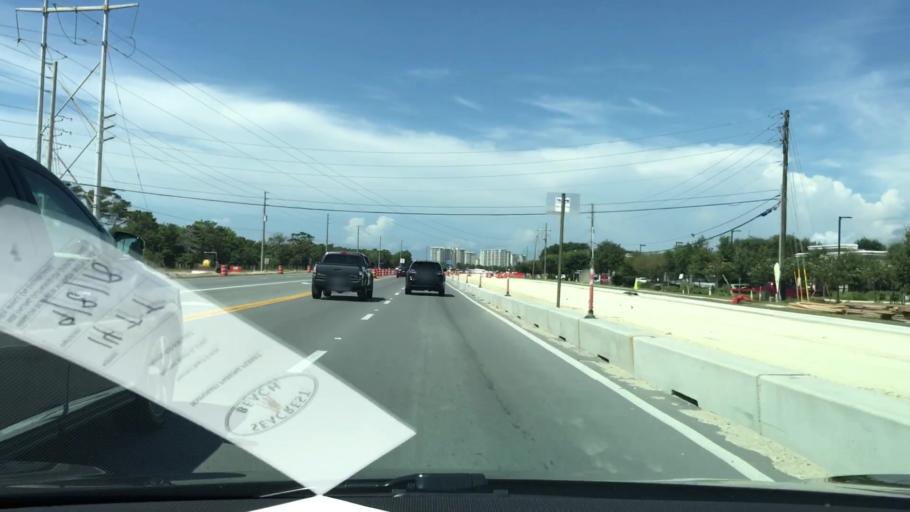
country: US
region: Florida
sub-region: Okaloosa County
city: Destin
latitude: 30.3878
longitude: -86.4357
